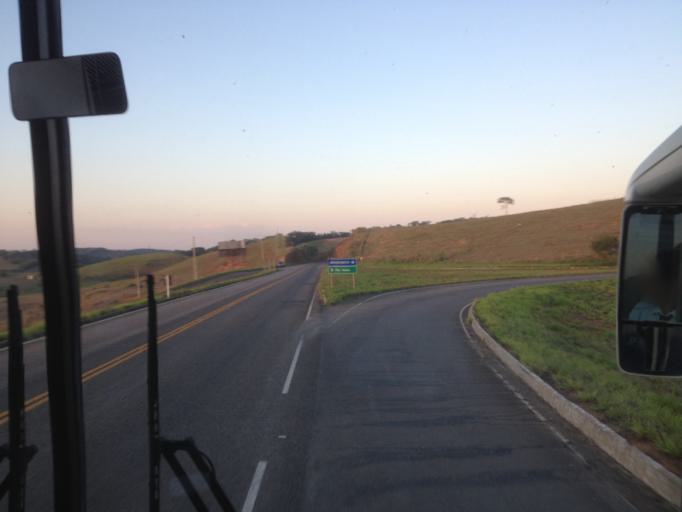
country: BR
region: Minas Gerais
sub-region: Rio Novo
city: Rio Novo
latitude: -21.5121
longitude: -43.1601
